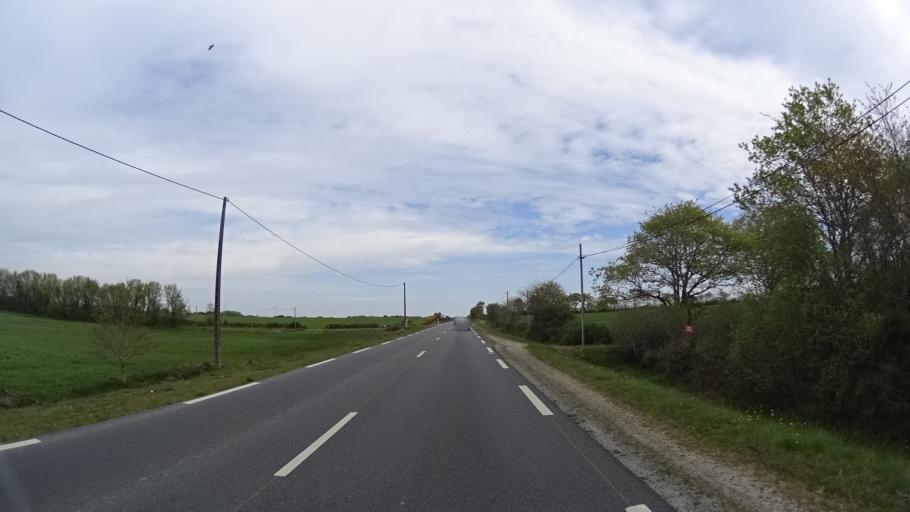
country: FR
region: Pays de la Loire
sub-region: Departement de la Loire-Atlantique
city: Bourgneuf-en-Retz
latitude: 47.0484
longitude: -1.9354
